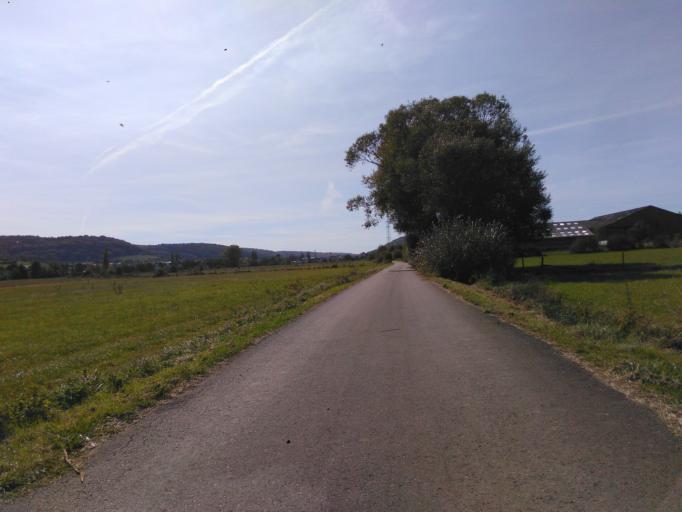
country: LU
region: Luxembourg
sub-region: Canton d'Esch-sur-Alzette
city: Kayl
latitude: 49.5000
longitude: 6.0474
